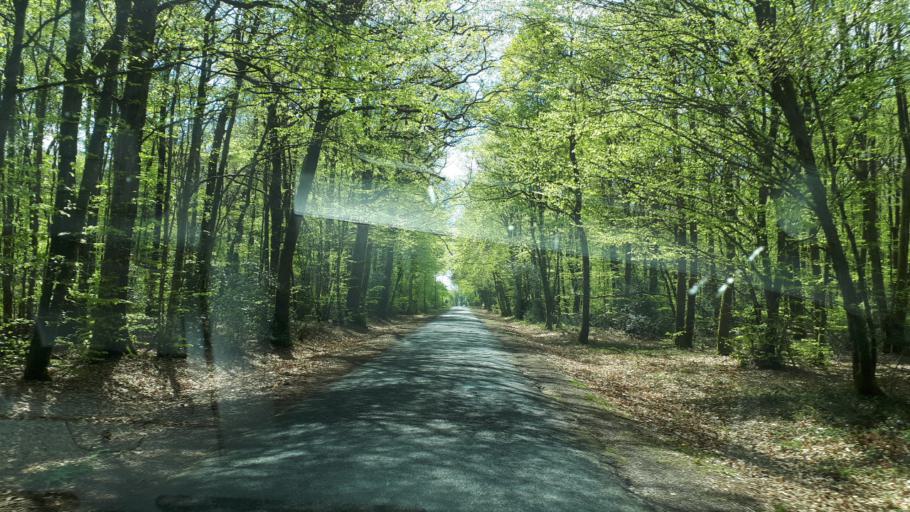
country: FR
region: Centre
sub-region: Departement du Cher
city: Henrichemont
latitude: 47.2891
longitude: 2.5771
